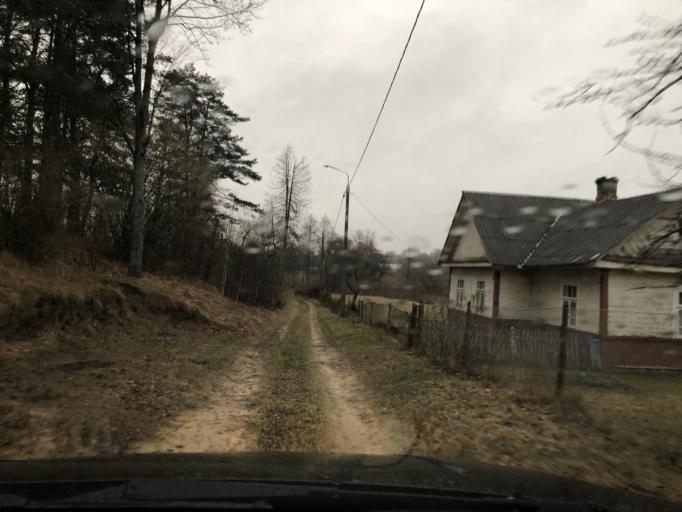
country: LT
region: Alytaus apskritis
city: Druskininkai
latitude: 53.9069
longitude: 24.1784
